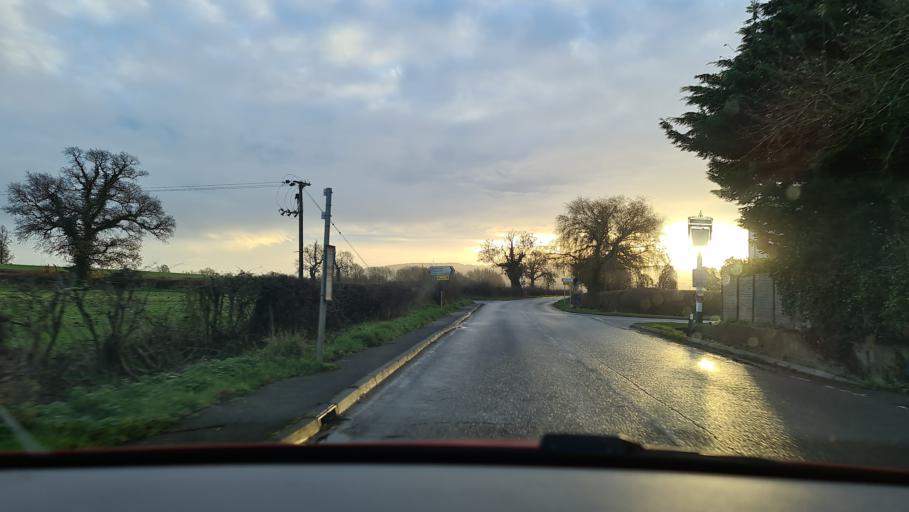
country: GB
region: England
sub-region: Oxfordshire
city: Chinnor
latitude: 51.7145
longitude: -0.9338
